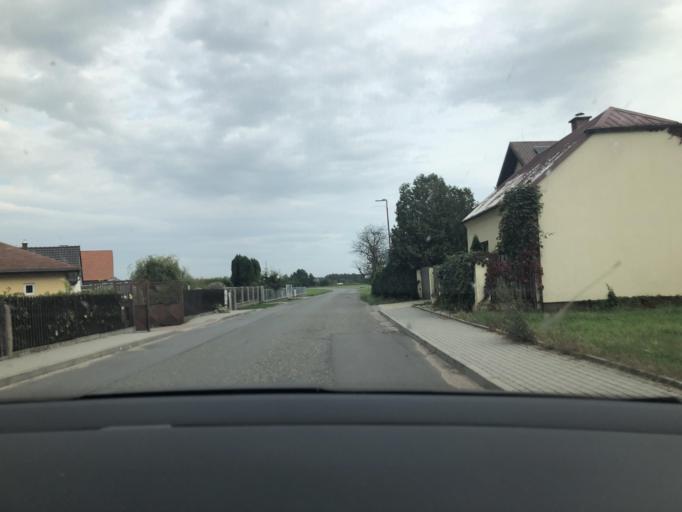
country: CZ
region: Pardubicky
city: Chvaletice
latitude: 50.0798
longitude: 15.4467
